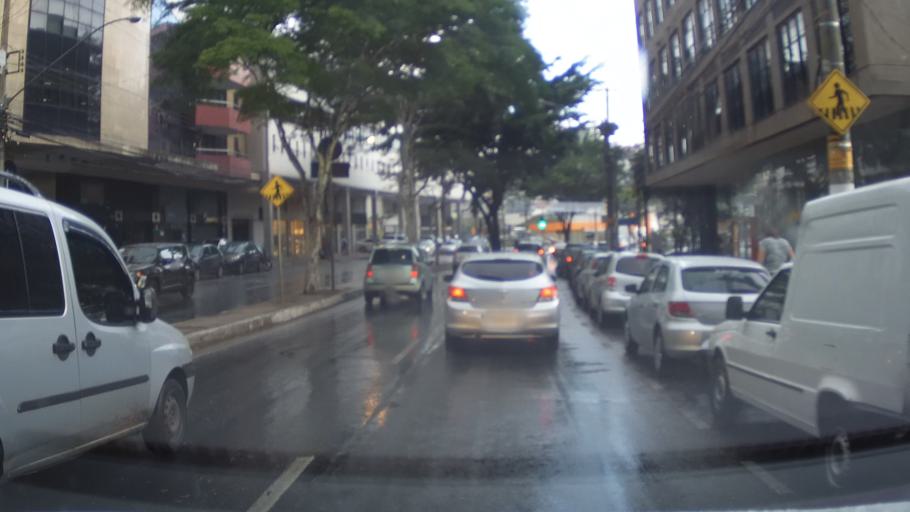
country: BR
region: Minas Gerais
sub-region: Belo Horizonte
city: Belo Horizonte
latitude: -19.9649
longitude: -43.9547
